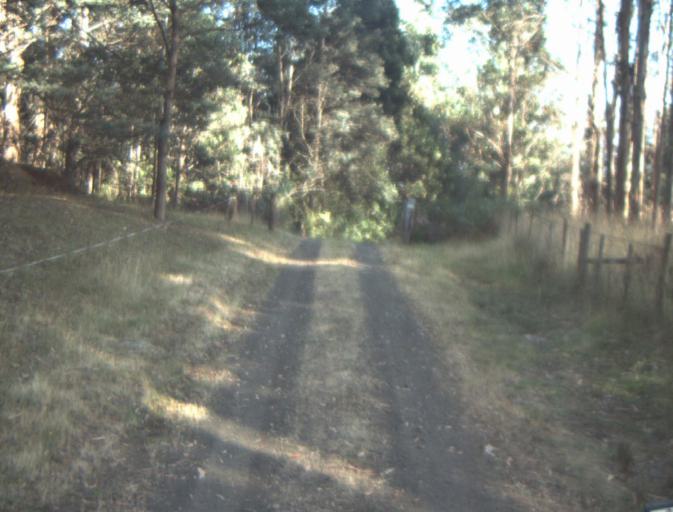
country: AU
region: Tasmania
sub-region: Launceston
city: Mayfield
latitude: -41.2852
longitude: 147.1884
